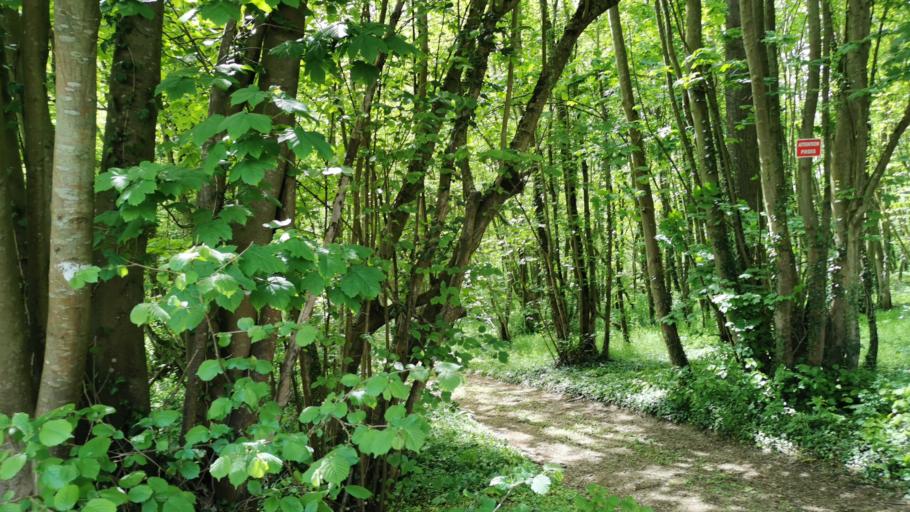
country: FR
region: Picardie
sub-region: Departement de la Somme
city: Doingt
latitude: 49.9319
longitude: 3.0288
